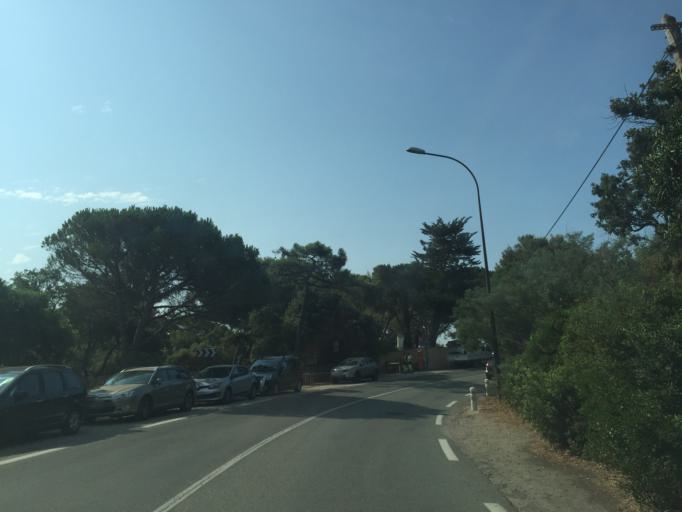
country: FR
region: Provence-Alpes-Cote d'Azur
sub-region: Departement du Var
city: Sainte-Maxime
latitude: 43.3139
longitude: 6.6695
